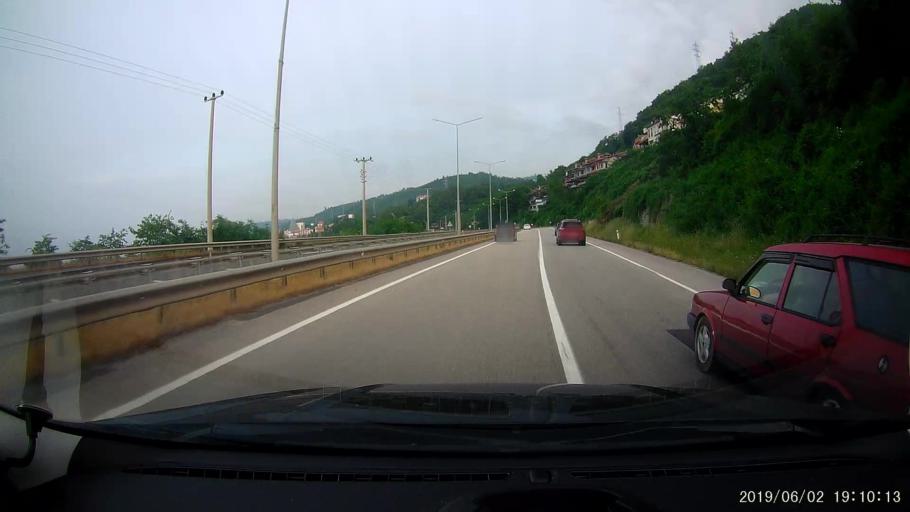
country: TR
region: Ordu
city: Gulyali
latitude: 40.9707
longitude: 38.0413
